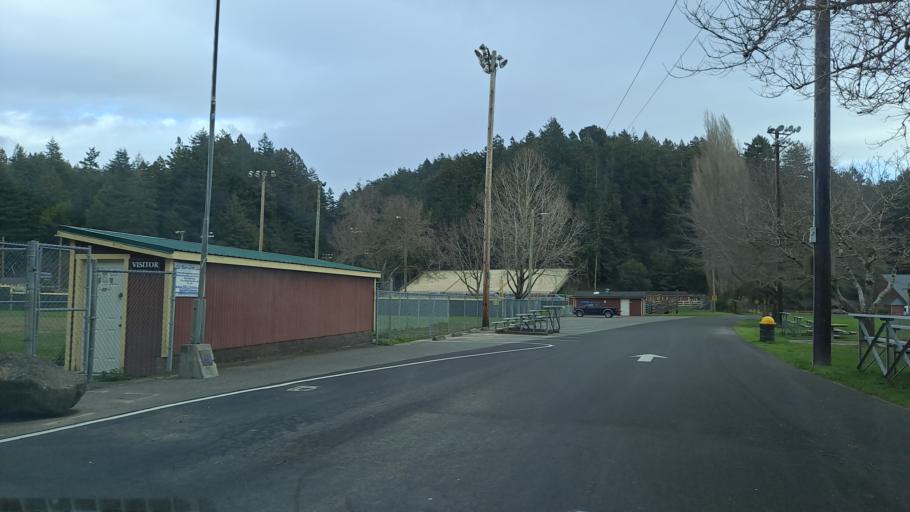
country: US
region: California
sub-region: Humboldt County
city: Fortuna
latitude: 40.6017
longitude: -124.1516
